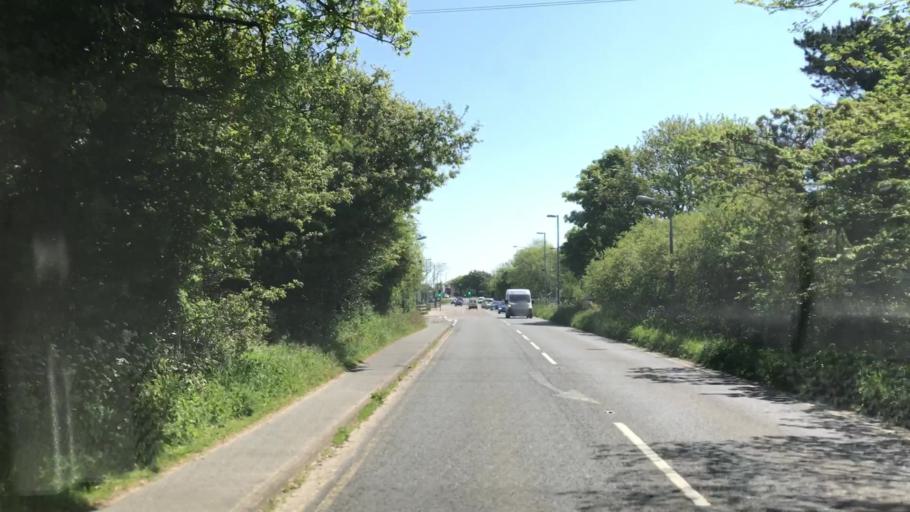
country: GB
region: England
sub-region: Cornwall
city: Chacewater
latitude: 50.2638
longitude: -5.1228
